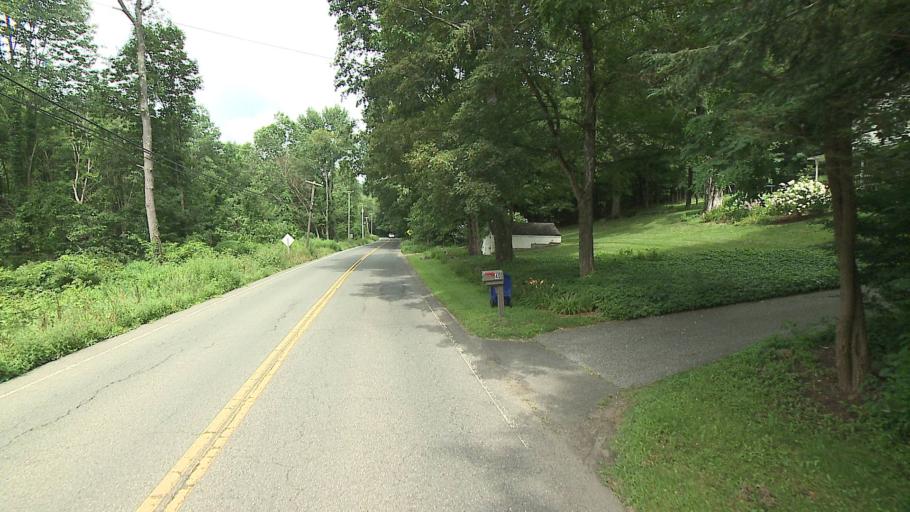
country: US
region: Connecticut
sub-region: Fairfield County
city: Sherman
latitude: 41.6468
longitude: -73.5050
